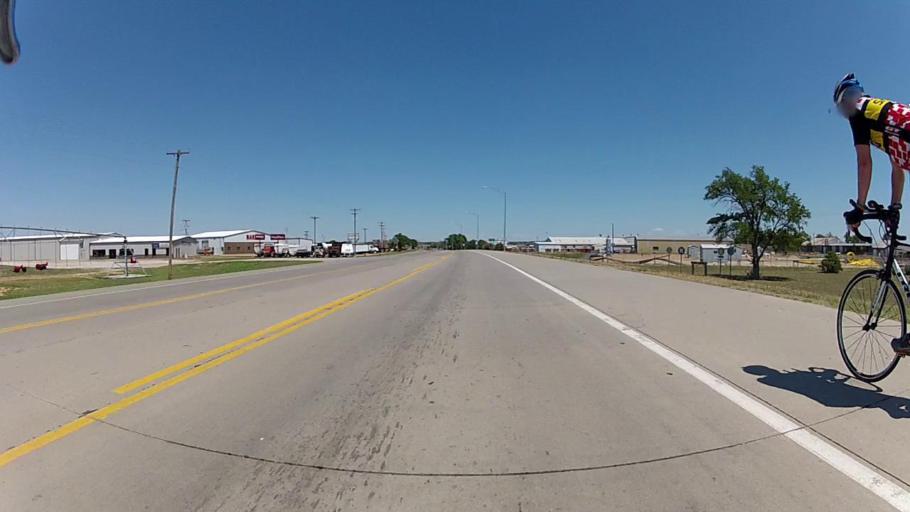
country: US
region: Kansas
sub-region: Ford County
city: Dodge City
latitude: 37.7243
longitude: -100.0156
